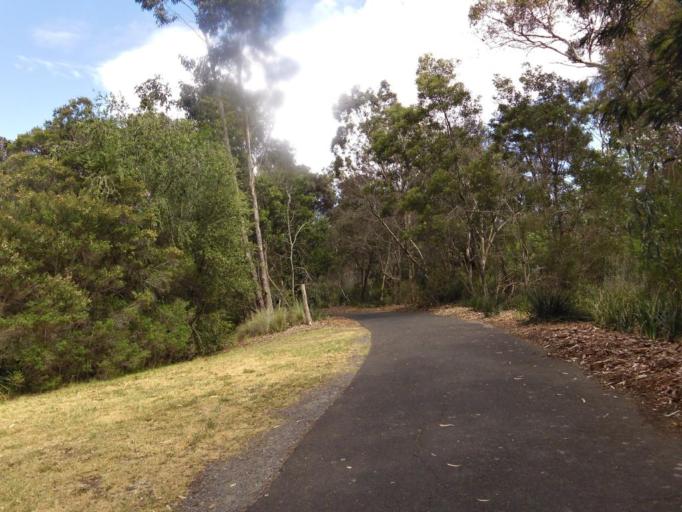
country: AU
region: Victoria
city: Carnegie
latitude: -37.8811
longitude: 145.0721
